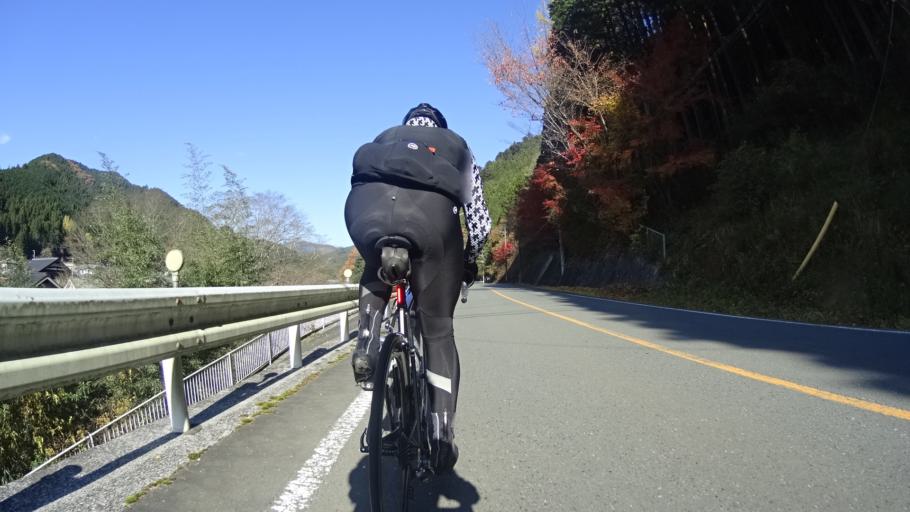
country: JP
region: Tokyo
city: Ome
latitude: 35.8854
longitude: 139.1825
